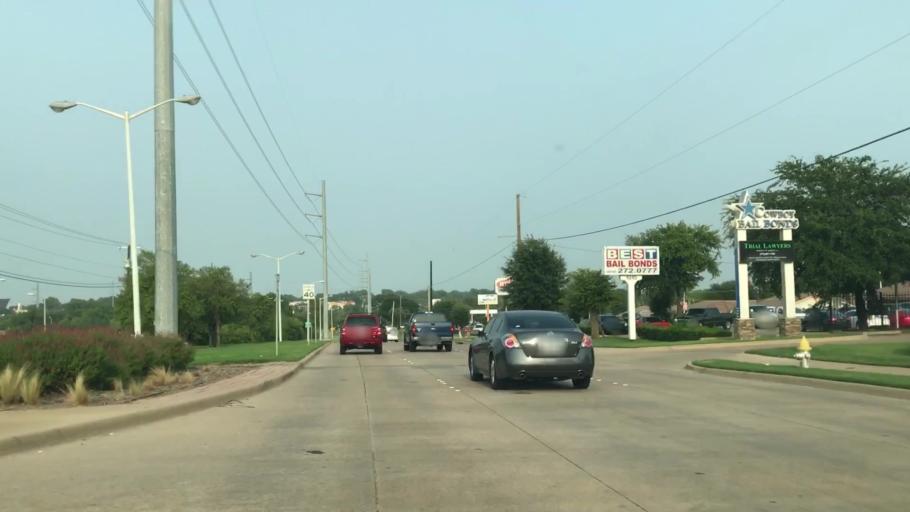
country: US
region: Texas
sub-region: Dallas County
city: Garland
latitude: 32.9089
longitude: -96.6566
